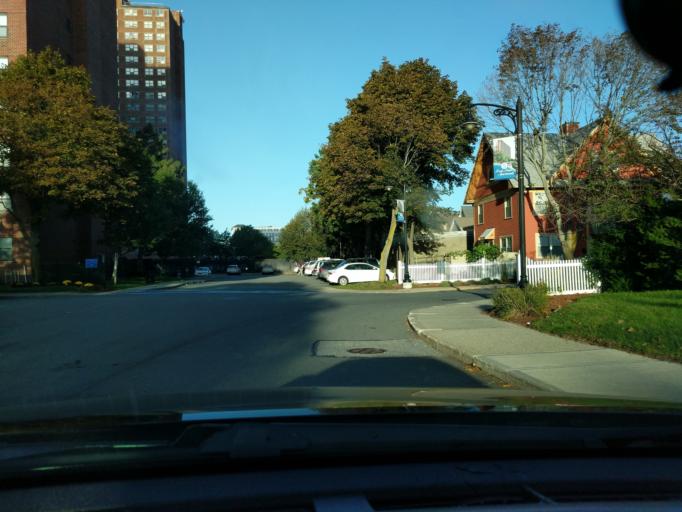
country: US
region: Massachusetts
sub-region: Middlesex County
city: Arlington
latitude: 42.3935
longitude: -71.1384
